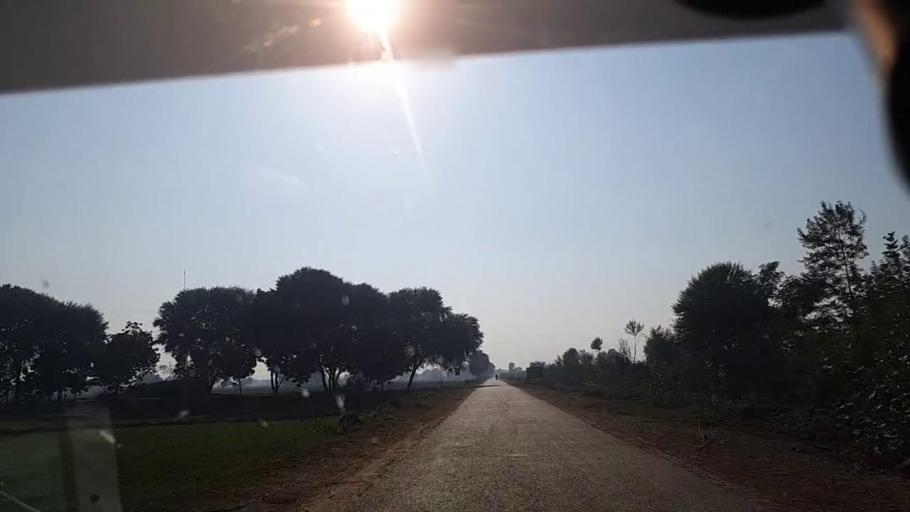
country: PK
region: Sindh
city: Sobhadero
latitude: 27.2457
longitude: 68.2905
